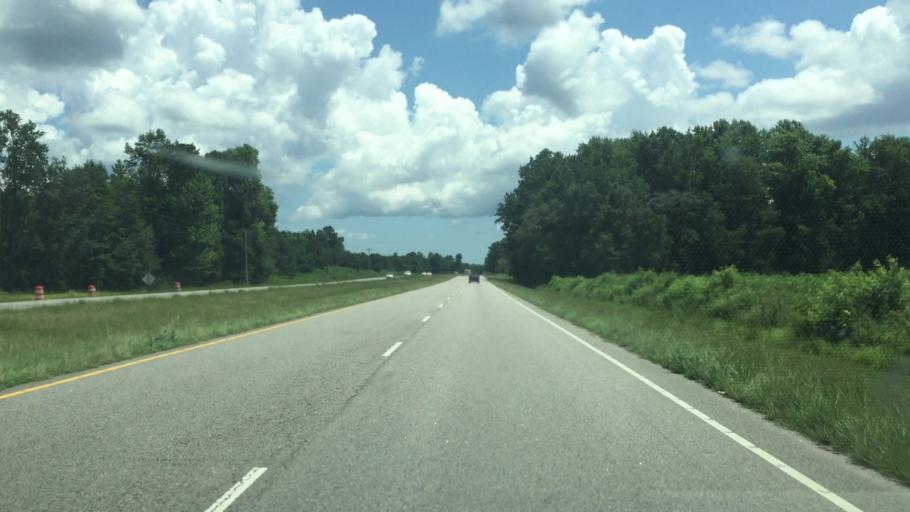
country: US
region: South Carolina
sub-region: Horry County
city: Loris
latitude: 34.0054
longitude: -78.7612
